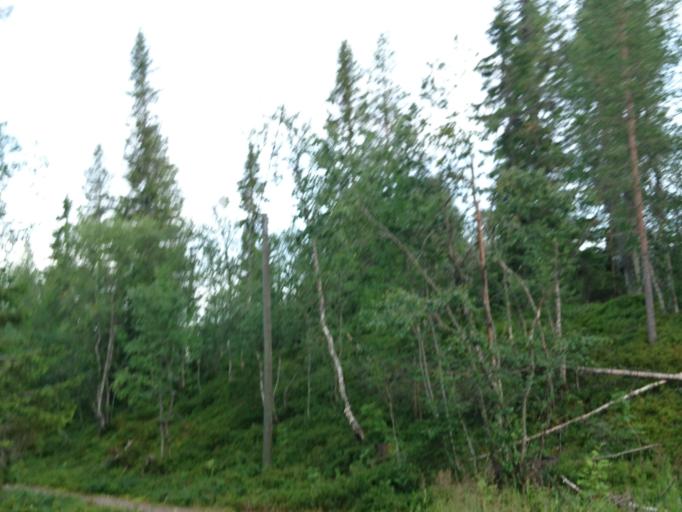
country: SE
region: Dalarna
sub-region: Malung-Saelens kommun
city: Malung
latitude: 61.1718
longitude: 13.1697
